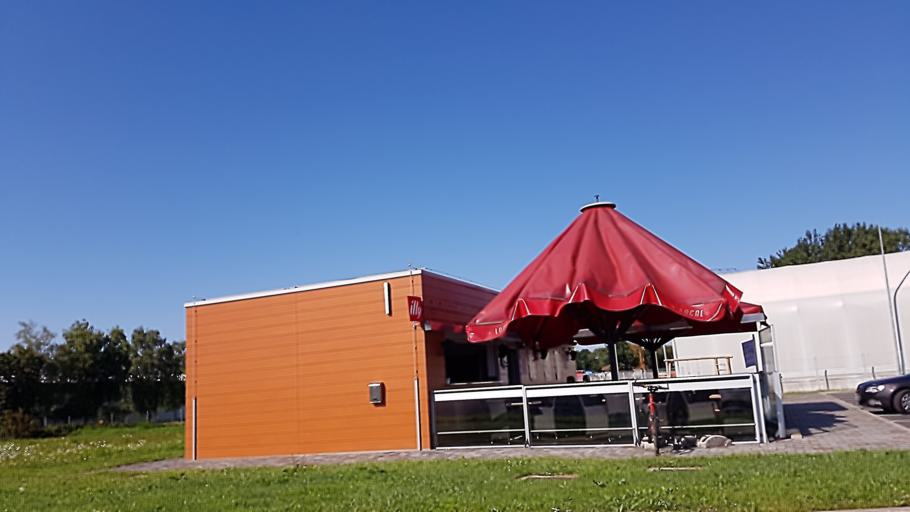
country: SI
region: Ljutomer
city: Ljutomer
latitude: 46.5303
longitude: 16.1899
